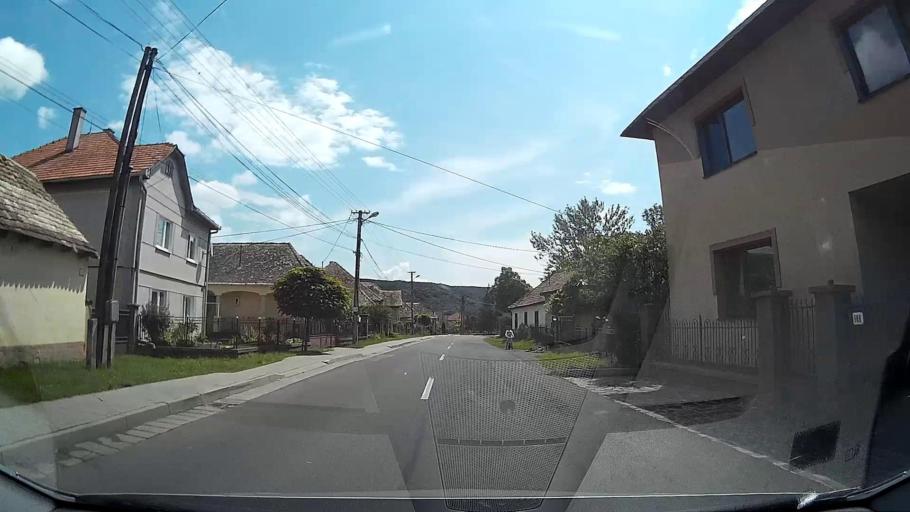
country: SK
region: Banskobystricky
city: Fil'akovo
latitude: 48.3482
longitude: 19.8385
